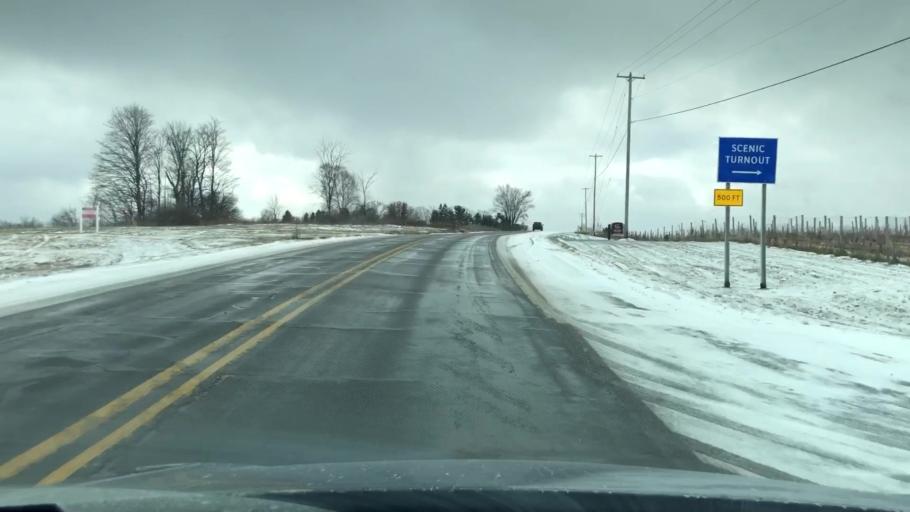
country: US
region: Michigan
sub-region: Antrim County
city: Elk Rapids
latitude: 44.8650
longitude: -85.5173
